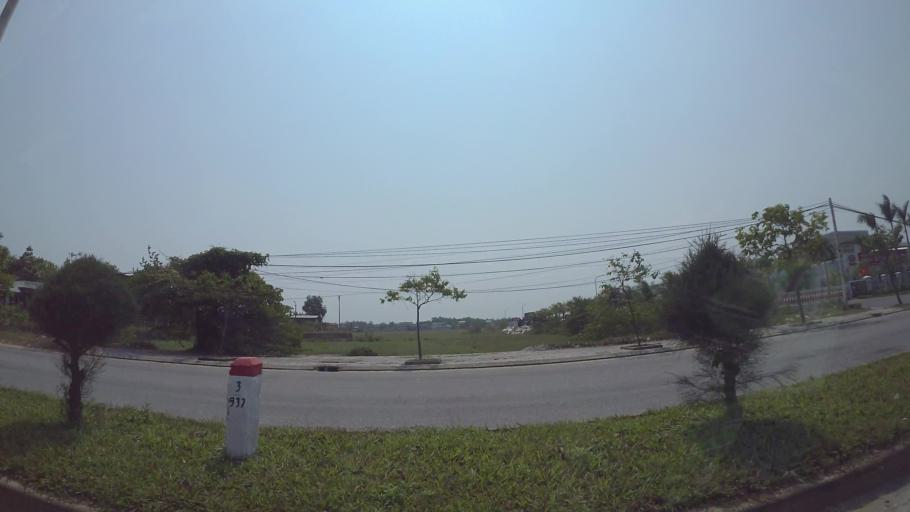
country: VN
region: Da Nang
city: Cam Le
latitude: 15.9844
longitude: 108.2036
